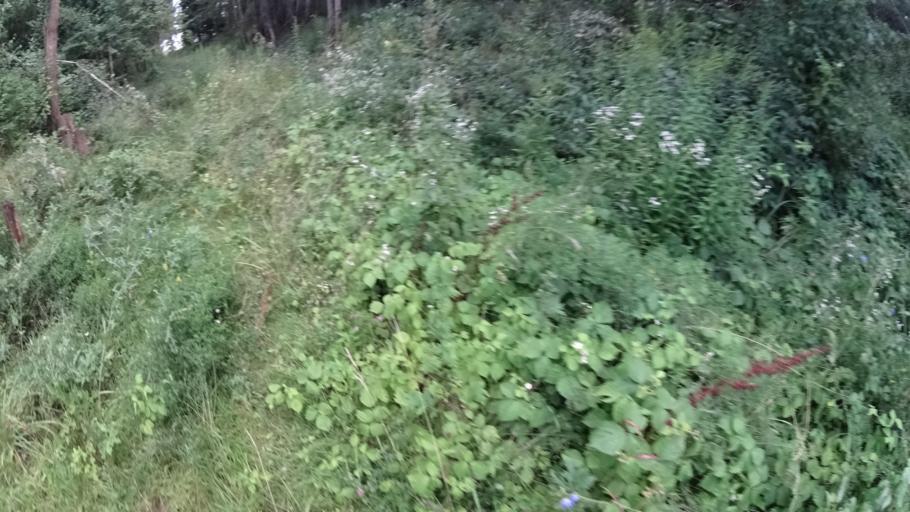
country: PL
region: Masovian Voivodeship
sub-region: Powiat piaseczynski
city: Tarczyn
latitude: 51.9691
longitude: 20.8689
